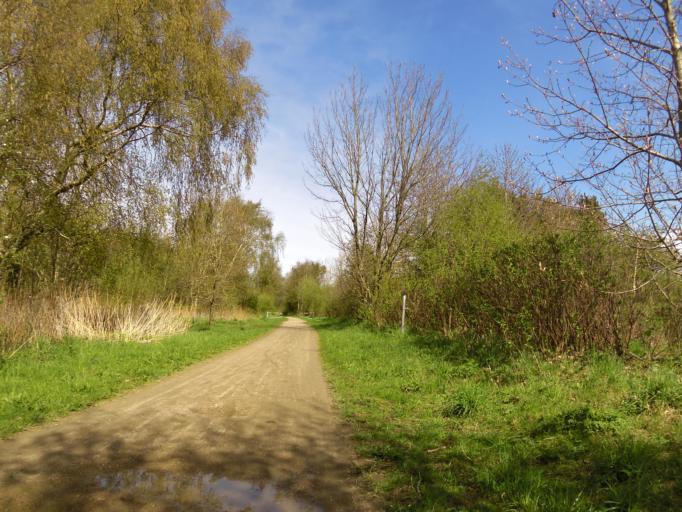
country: DK
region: Central Jutland
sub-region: Skive Kommune
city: Skive
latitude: 56.5776
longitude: 9.0232
